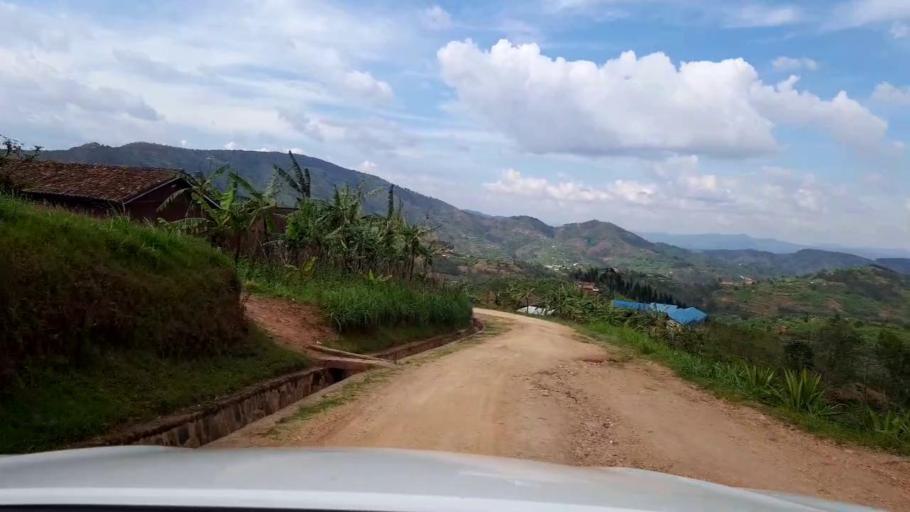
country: RW
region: Southern Province
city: Gitarama
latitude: -1.9794
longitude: 29.7109
